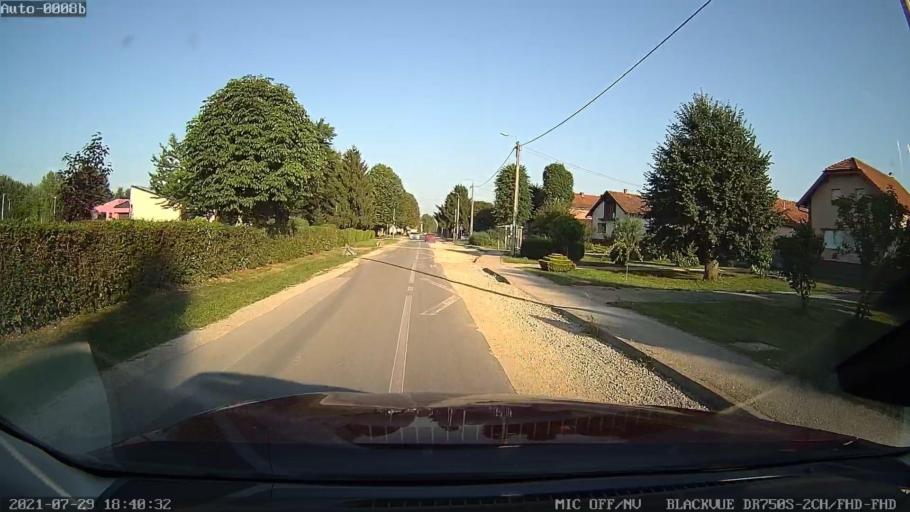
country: HR
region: Varazdinska
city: Petrijanec
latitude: 46.3195
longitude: 16.2297
